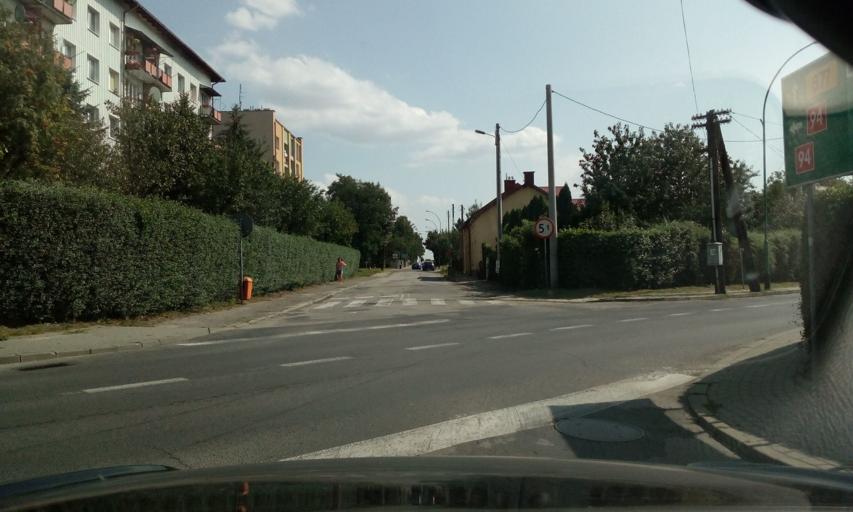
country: PL
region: Subcarpathian Voivodeship
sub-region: Powiat lancucki
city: Lancut
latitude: 50.0636
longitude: 22.2285
